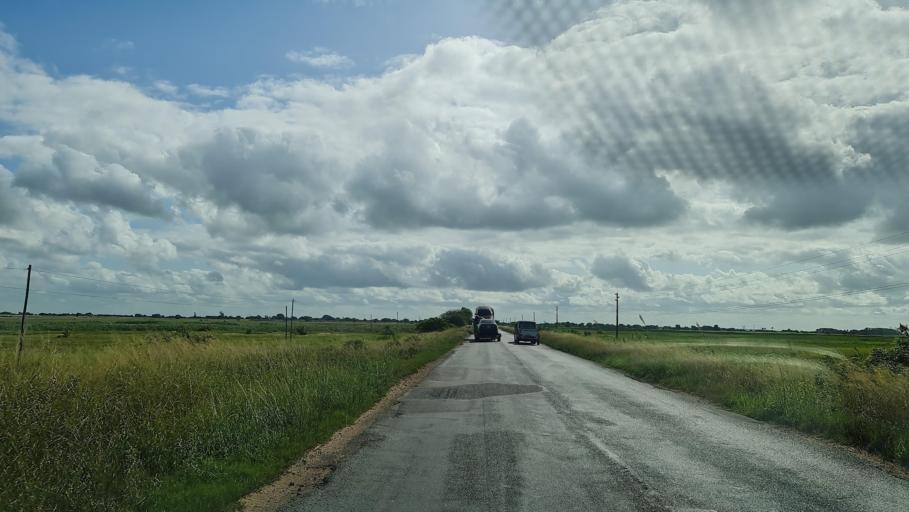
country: MZ
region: Gaza
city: Macia
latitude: -25.0976
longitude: 32.8283
